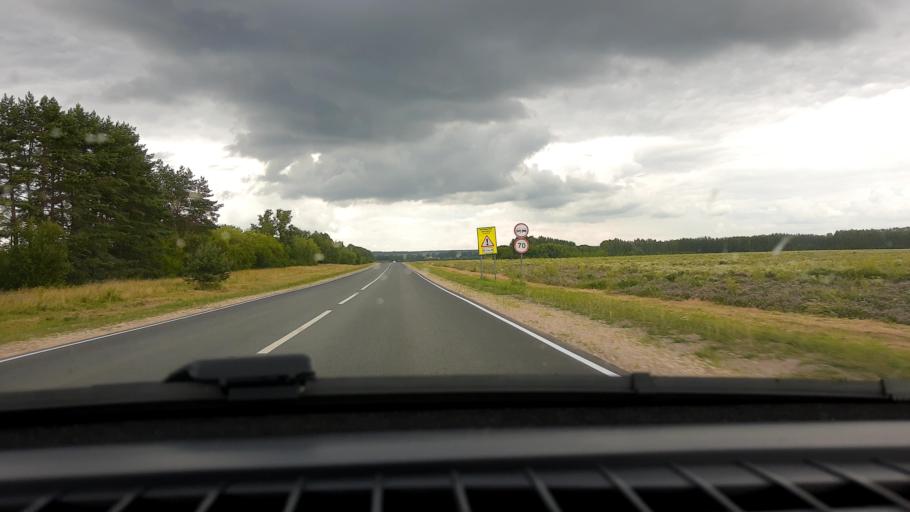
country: RU
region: Nizjnij Novgorod
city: Bol'shoye Murashkino
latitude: 55.8630
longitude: 44.7484
